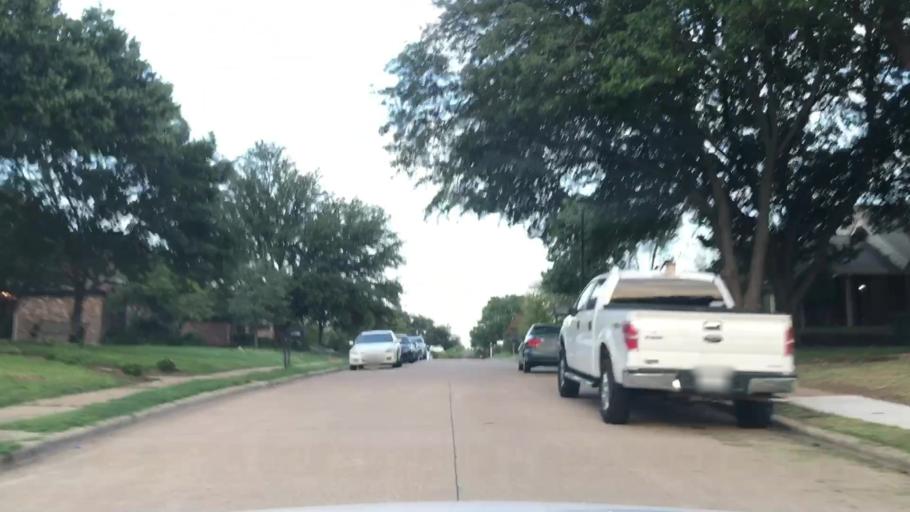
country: US
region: Texas
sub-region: Dallas County
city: Addison
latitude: 33.0048
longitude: -96.8603
